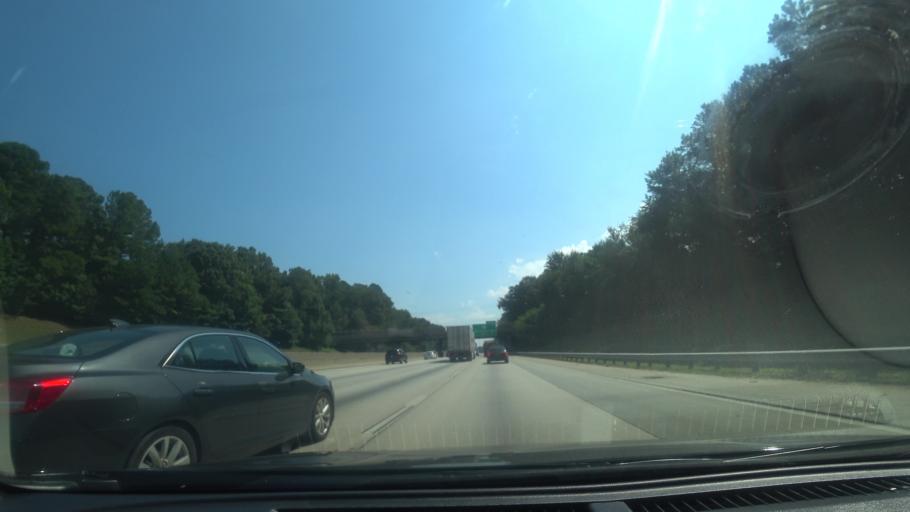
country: US
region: Georgia
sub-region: DeKalb County
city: Avondale Estates
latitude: 33.7649
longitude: -84.2326
